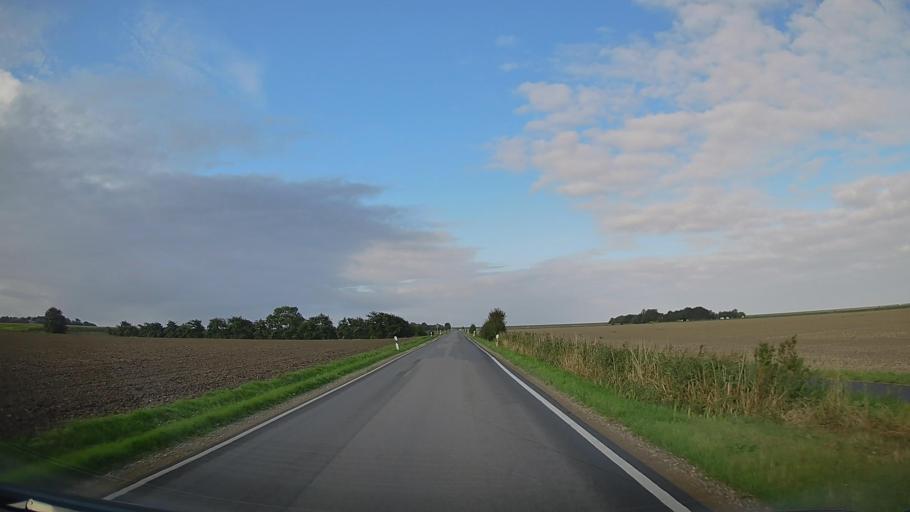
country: DE
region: Schleswig-Holstein
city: Reussenkoge
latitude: 54.5714
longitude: 8.9380
